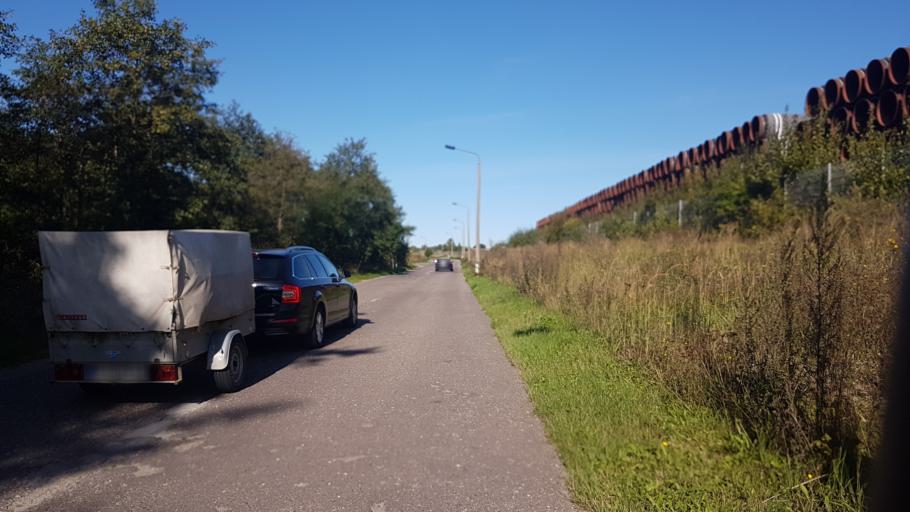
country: DE
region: Mecklenburg-Vorpommern
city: Sagard
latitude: 54.4905
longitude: 13.5715
